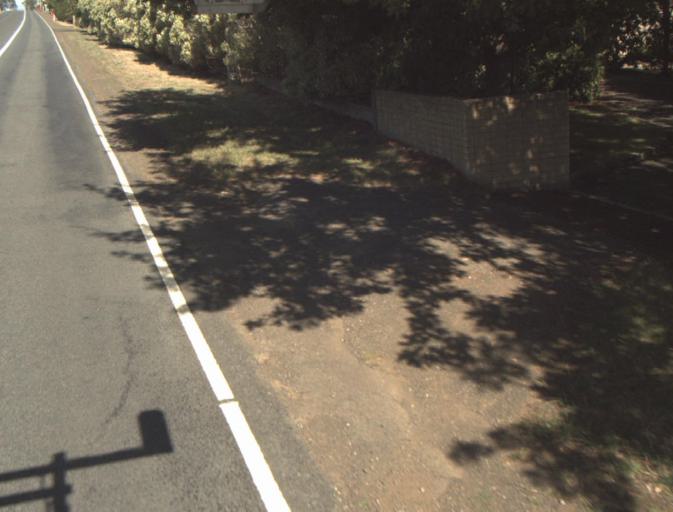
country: AU
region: Tasmania
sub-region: Launceston
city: Mayfield
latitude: -41.3346
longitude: 147.0780
